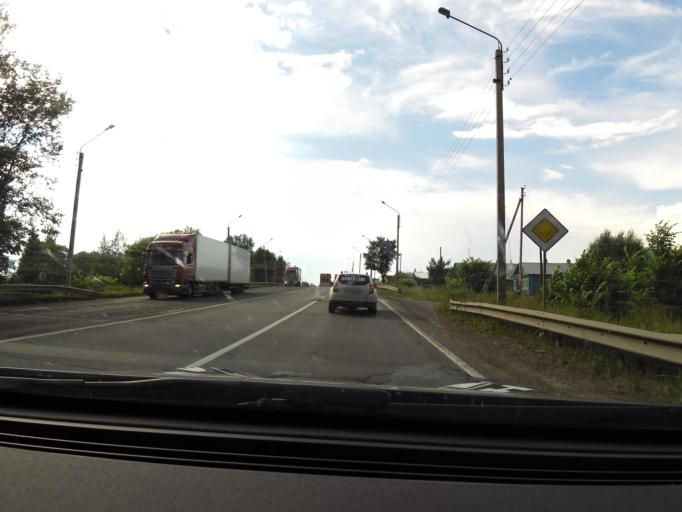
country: RU
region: Vladimir
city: Novovyazniki
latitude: 56.1810
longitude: 42.4074
